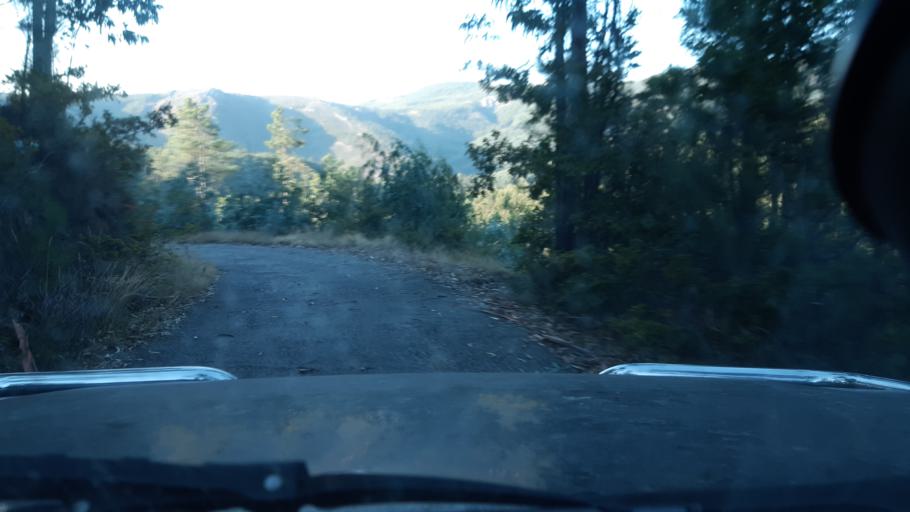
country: PT
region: Viseu
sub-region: Mortagua
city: Mortagua
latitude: 40.5226
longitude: -8.2523
